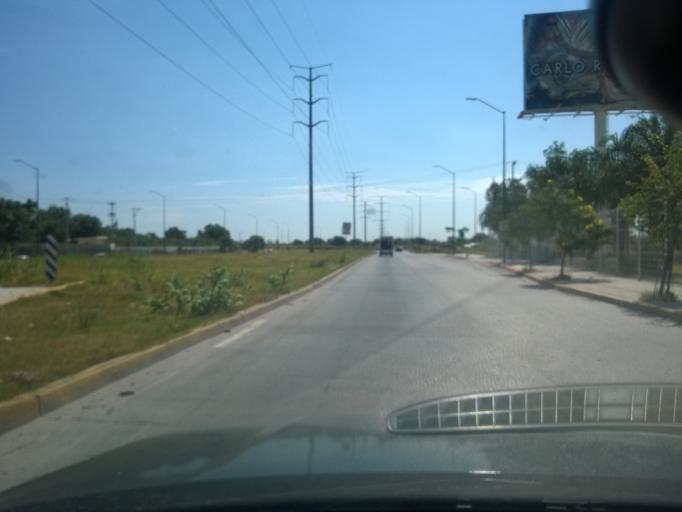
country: MX
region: Guanajuato
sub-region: Leon
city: San Jose de Duran (Los Troncoso)
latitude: 21.0958
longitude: -101.7051
